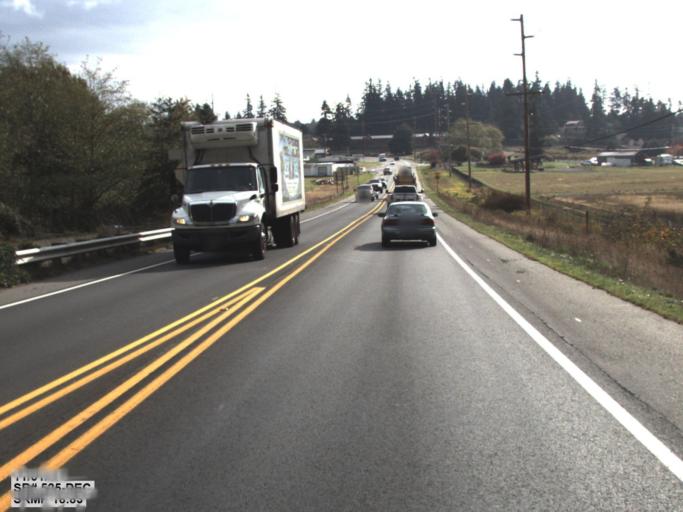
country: US
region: Washington
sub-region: Island County
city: Freeland
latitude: 48.0142
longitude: -122.5442
